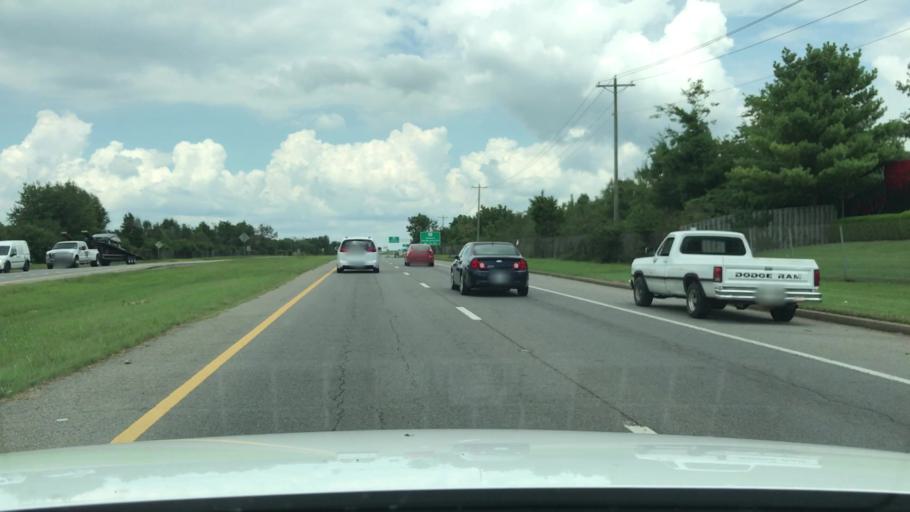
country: US
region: Tennessee
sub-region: Sumner County
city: Gallatin
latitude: 36.3728
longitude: -86.4634
